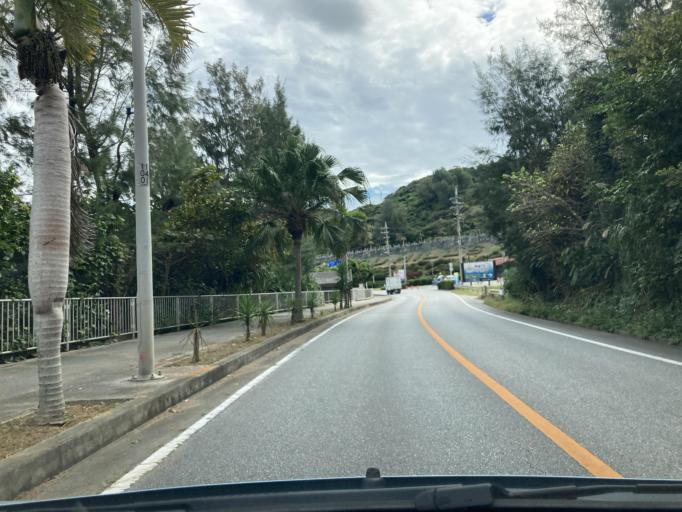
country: JP
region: Okinawa
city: Ishikawa
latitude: 26.4356
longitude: 127.7819
